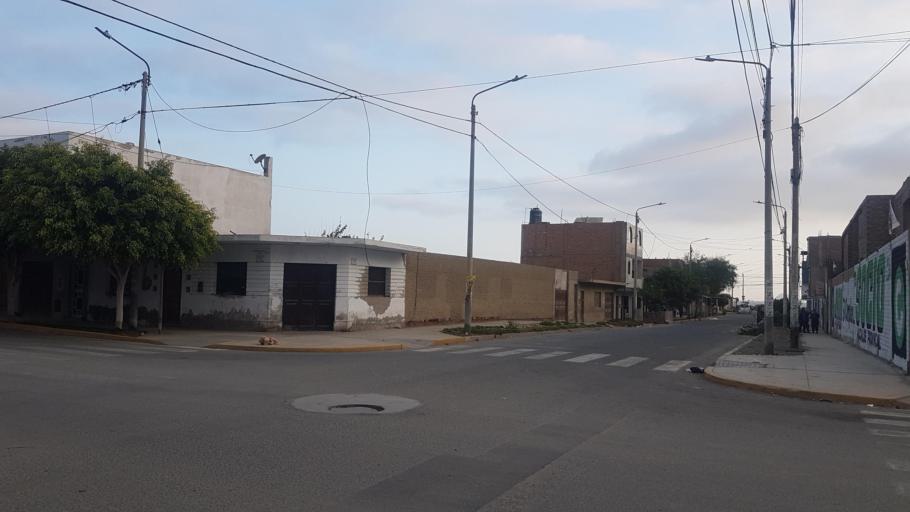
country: PE
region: Ancash
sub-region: Provincia de Santa
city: Chimbote
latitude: -9.0940
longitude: -78.5720
